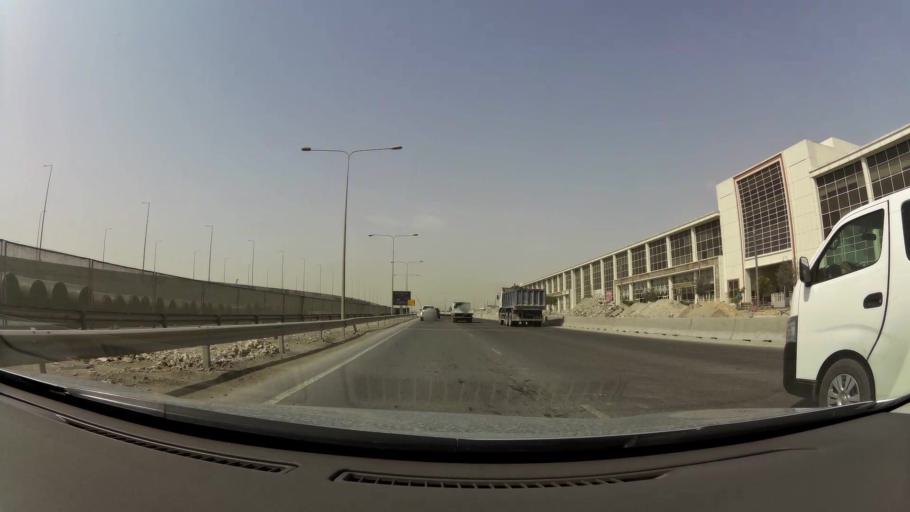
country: QA
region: Al Wakrah
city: Al Wukayr
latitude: 25.1945
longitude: 51.4592
